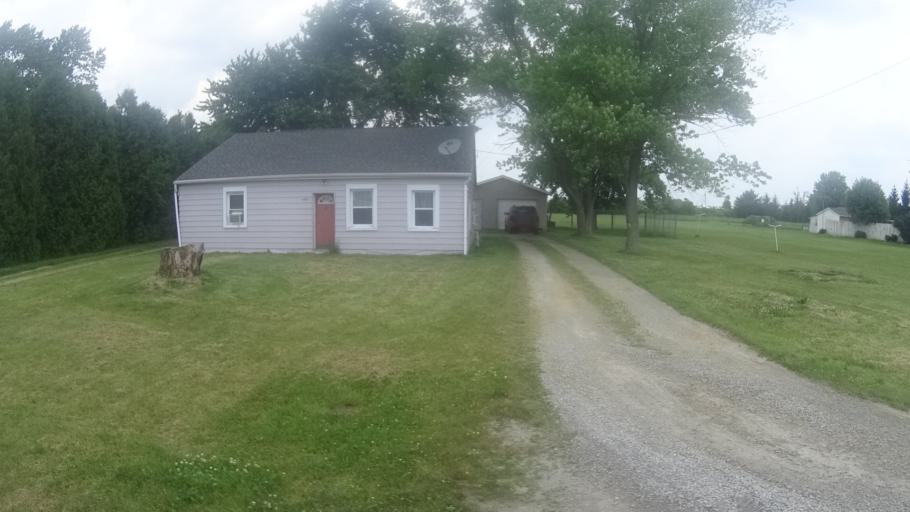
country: US
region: Ohio
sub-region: Huron County
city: Monroeville
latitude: 41.3110
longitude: -82.6947
